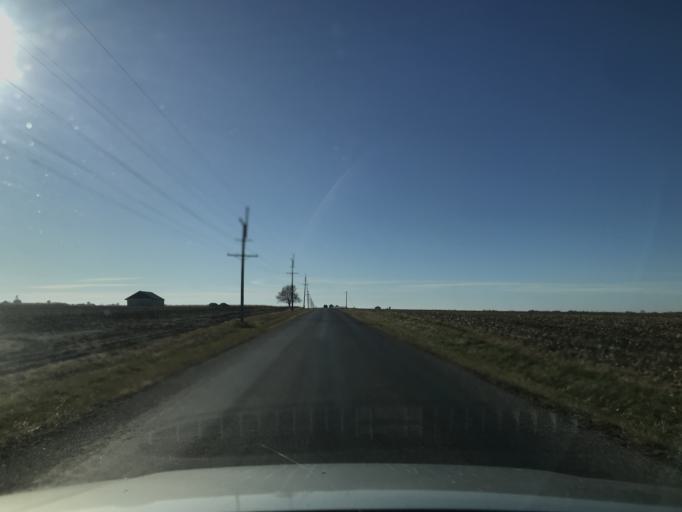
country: US
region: Illinois
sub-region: Hancock County
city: Carthage
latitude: 40.4856
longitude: -91.1780
